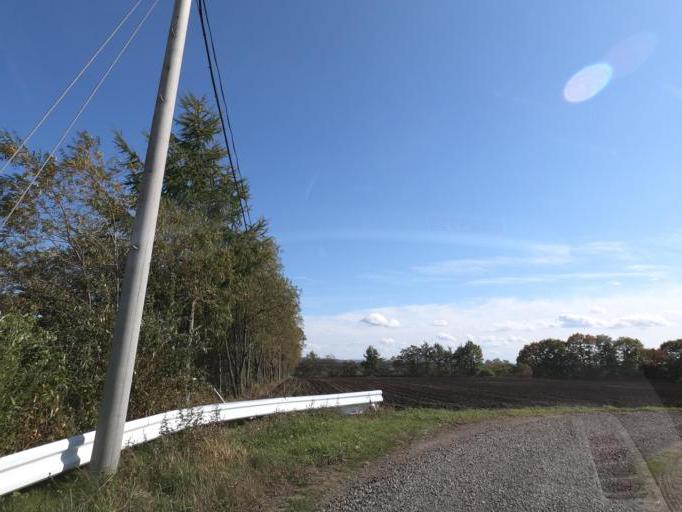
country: JP
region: Hokkaido
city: Otofuke
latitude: 43.2399
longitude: 143.2623
